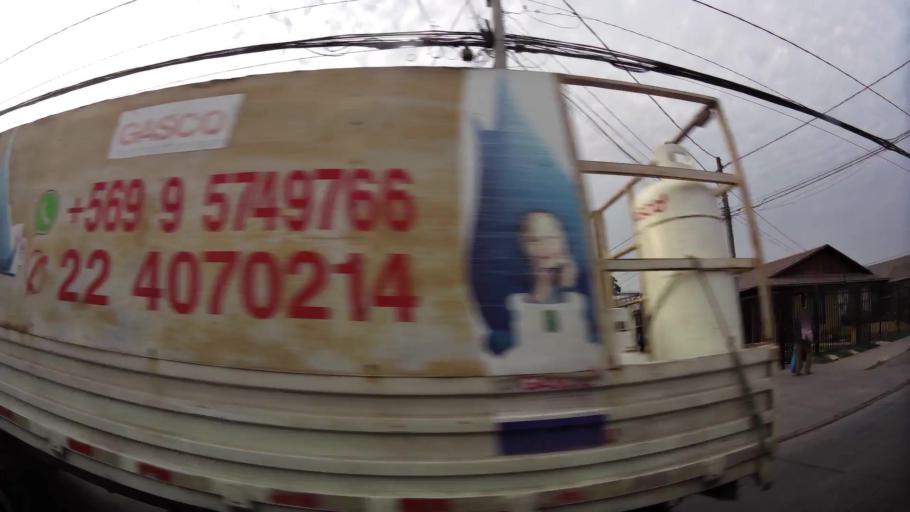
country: CL
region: Santiago Metropolitan
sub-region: Provincia de Santiago
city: Lo Prado
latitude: -33.5223
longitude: -70.7965
